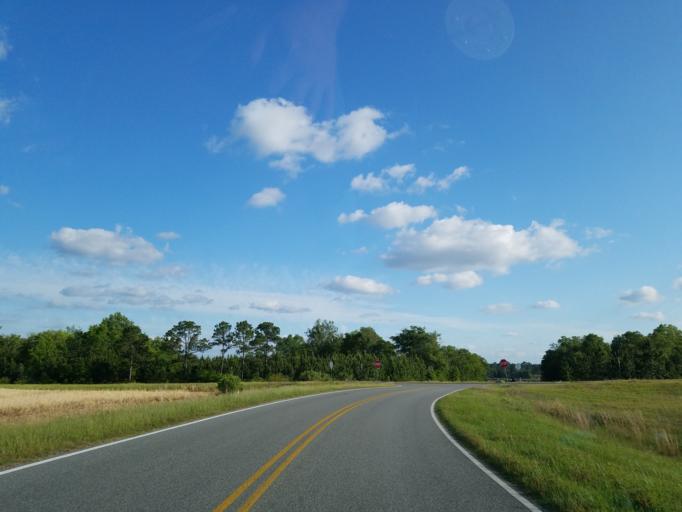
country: US
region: Georgia
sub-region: Turner County
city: Ashburn
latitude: 31.6090
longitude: -83.5626
